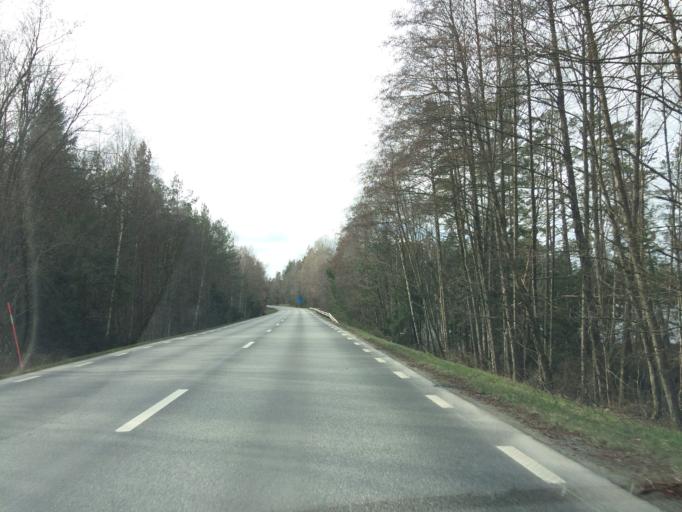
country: SE
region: Skane
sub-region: Osby Kommun
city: Lonsboda
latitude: 56.3803
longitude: 14.2626
